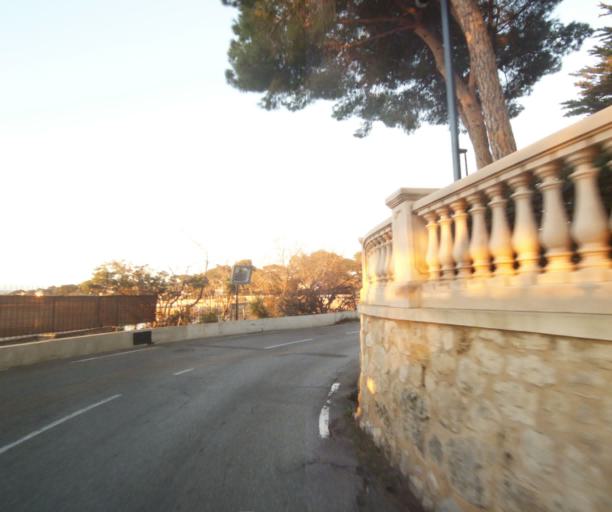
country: FR
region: Provence-Alpes-Cote d'Azur
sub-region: Departement des Alpes-Maritimes
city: Antibes
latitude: 43.5519
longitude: 7.1214
